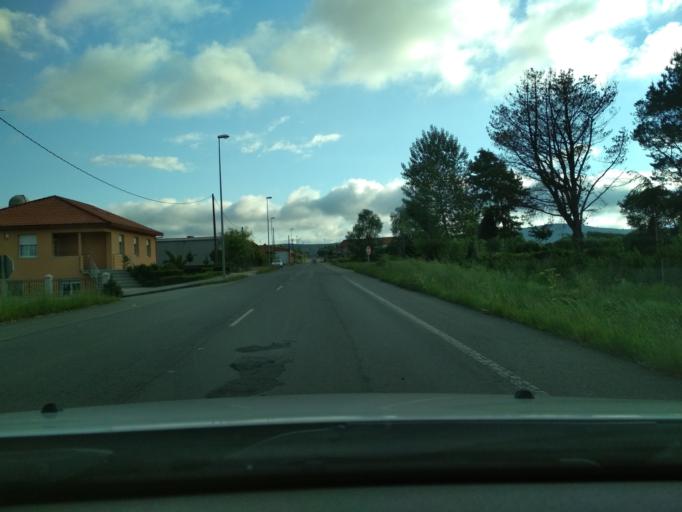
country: ES
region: Galicia
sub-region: Provincia da Coruna
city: Mazaricos
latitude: 42.9642
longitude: -8.9118
